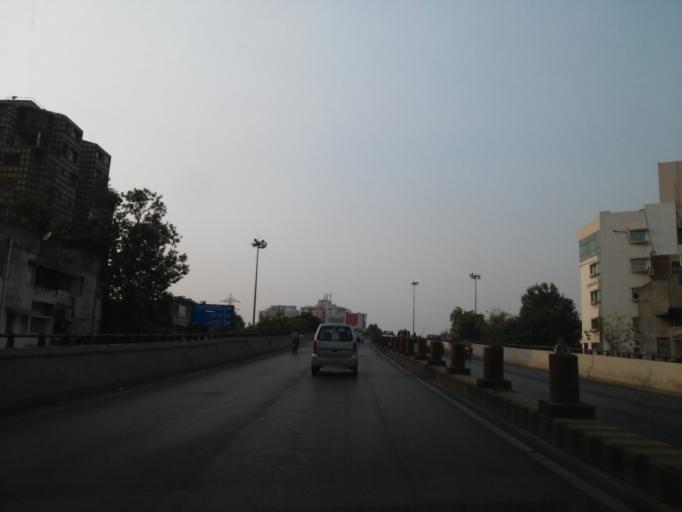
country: IN
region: Gujarat
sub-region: Ahmadabad
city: Ahmedabad
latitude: 23.0100
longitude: 72.5475
